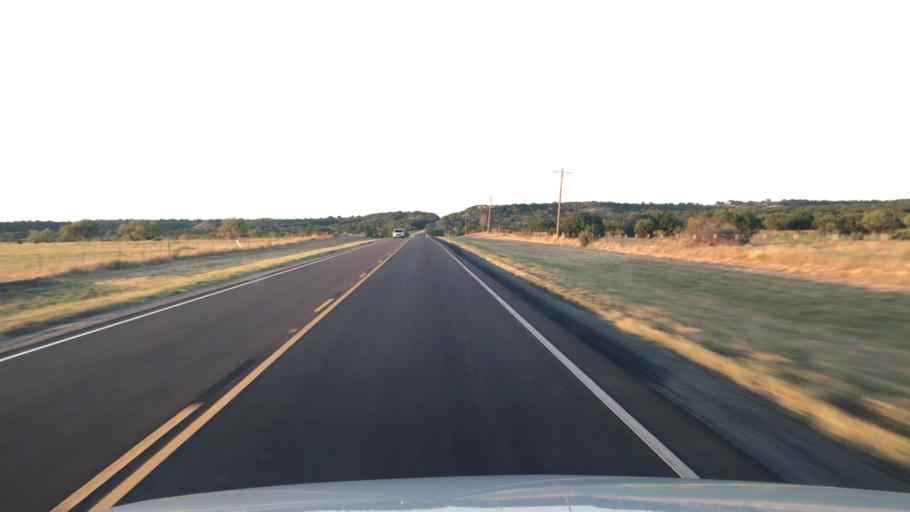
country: US
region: Texas
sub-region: Hamilton County
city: Hico
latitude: 32.0860
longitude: -97.9753
